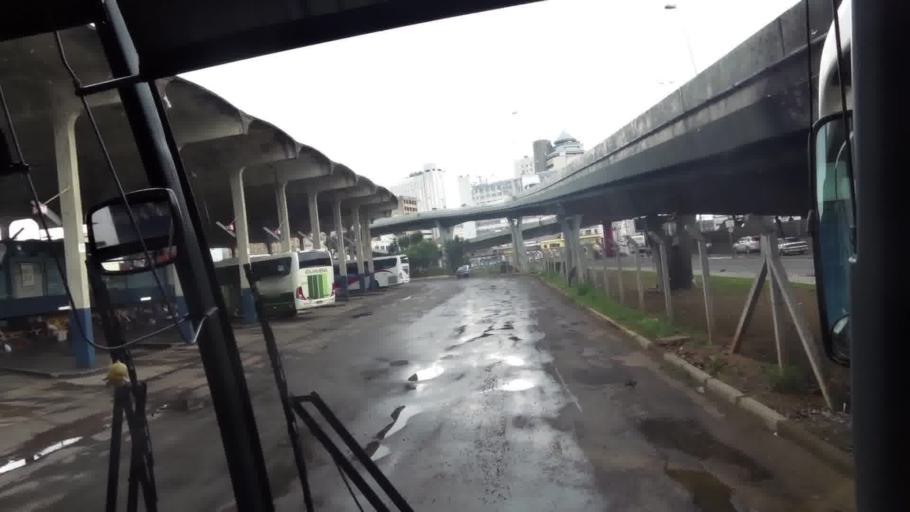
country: BR
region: Rio Grande do Sul
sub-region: Porto Alegre
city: Porto Alegre
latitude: -30.0223
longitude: -51.2195
